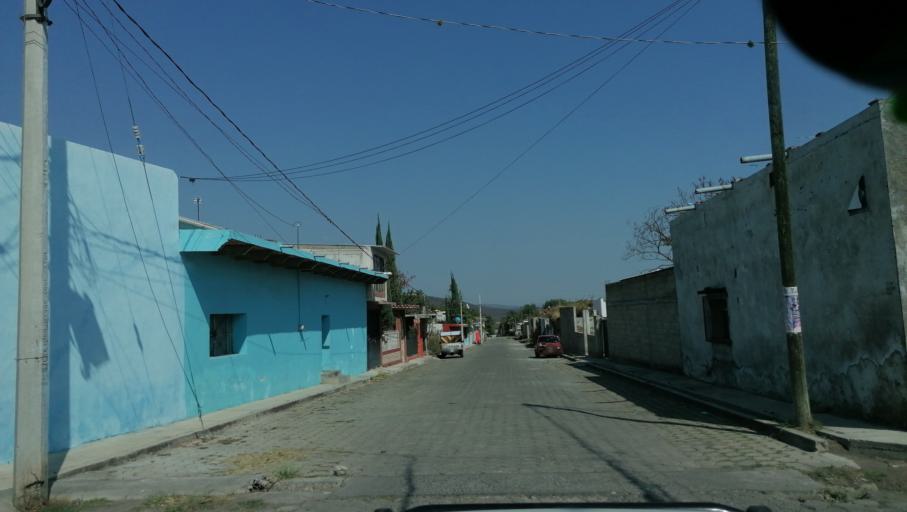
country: MX
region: Puebla
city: Huaquechula
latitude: 18.7724
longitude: -98.5422
